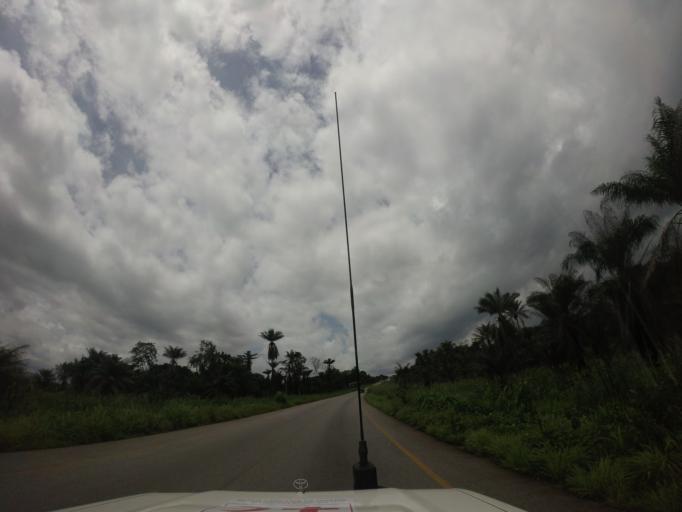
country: SL
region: Southern Province
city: Rotifunk
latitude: 8.4593
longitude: -12.6768
